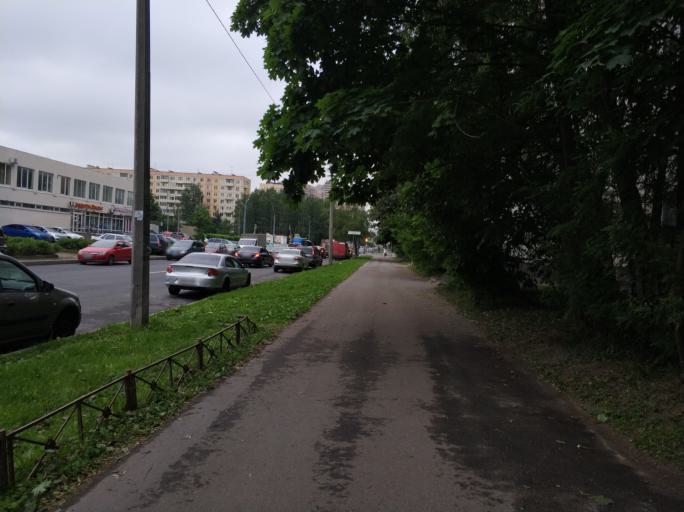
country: RU
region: St.-Petersburg
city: Grazhdanka
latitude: 60.0345
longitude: 30.3914
